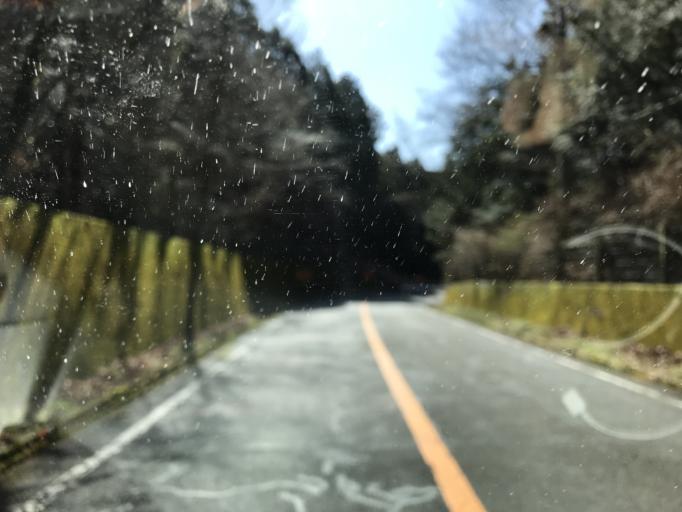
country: JP
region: Shizuoka
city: Fujinomiya
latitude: 35.2935
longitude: 138.6657
